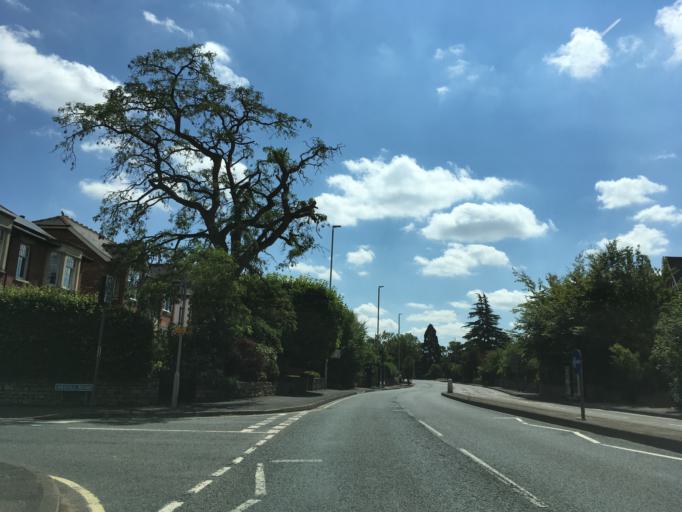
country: GB
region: England
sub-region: Gloucestershire
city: Gloucester
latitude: 51.8677
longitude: -2.2227
